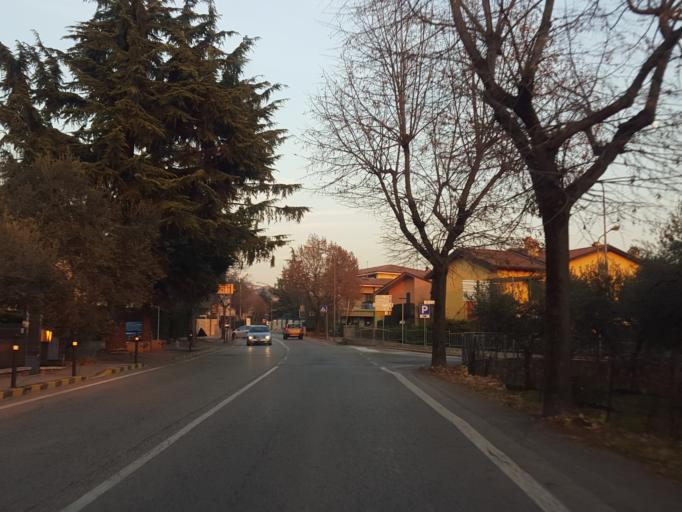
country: IT
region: Veneto
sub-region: Provincia di Verona
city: Garda
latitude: 45.5797
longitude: 10.7203
